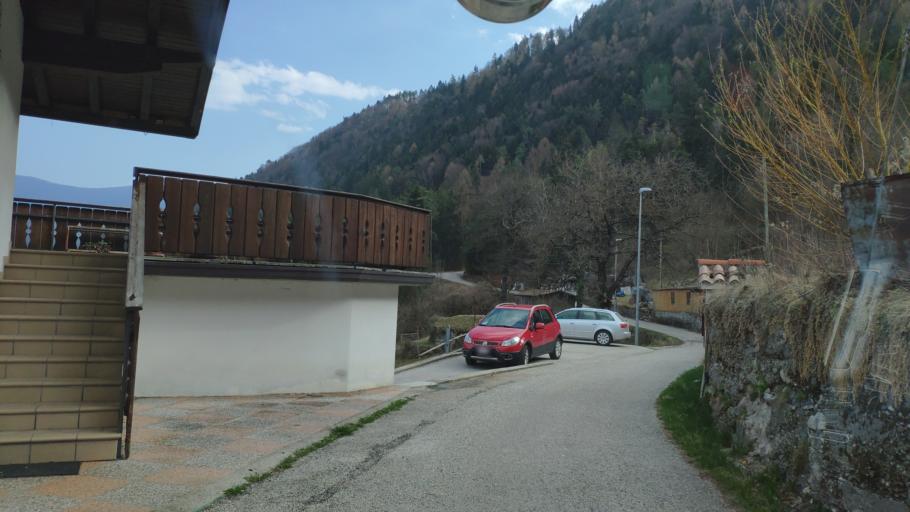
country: IT
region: Veneto
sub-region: Provincia di Vicenza
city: Enego
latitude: 45.9545
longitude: 11.7035
